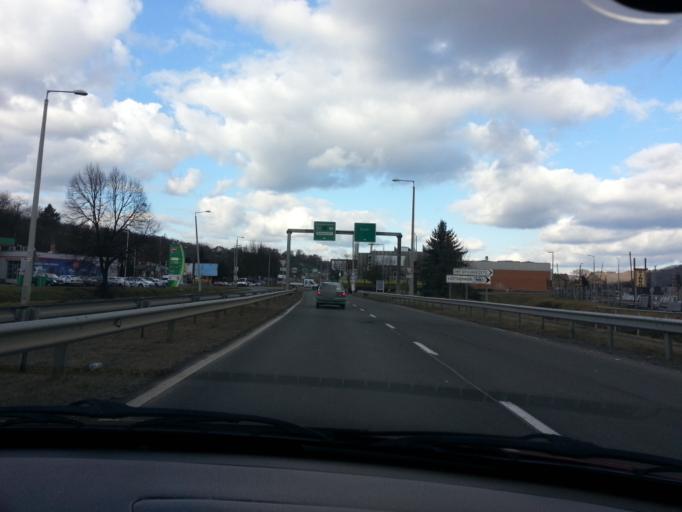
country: HU
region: Nograd
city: Salgotarjan
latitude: 48.0637
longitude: 19.7835
